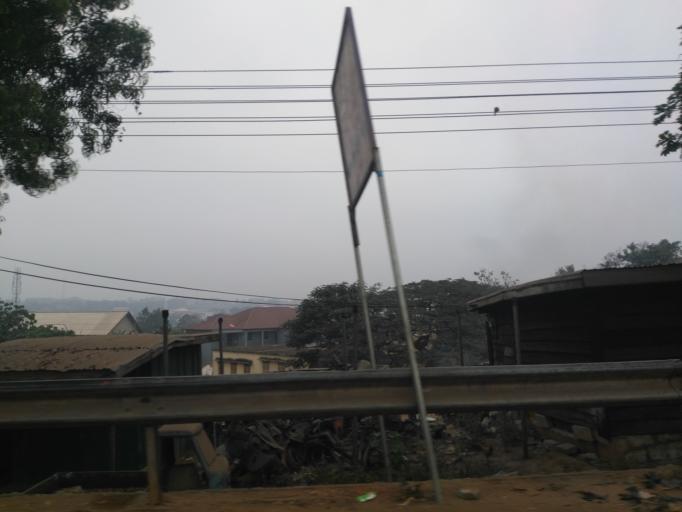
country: GH
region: Ashanti
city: Tafo
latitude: 6.7141
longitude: -1.6097
